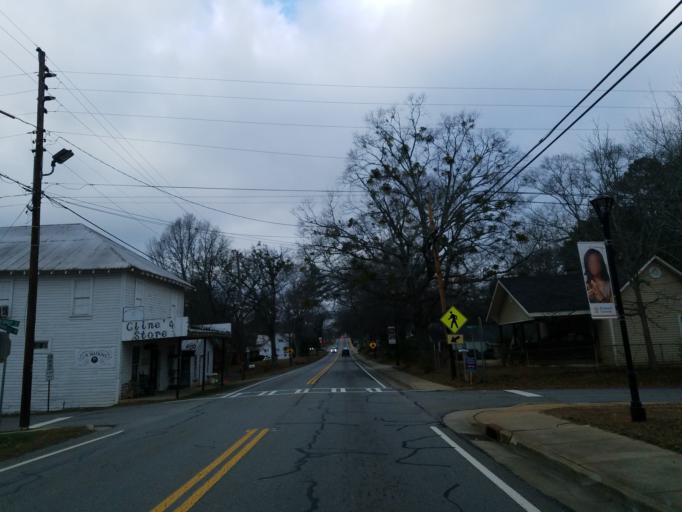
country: US
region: Georgia
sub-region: Cherokee County
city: Canton
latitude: 34.3154
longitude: -84.5509
